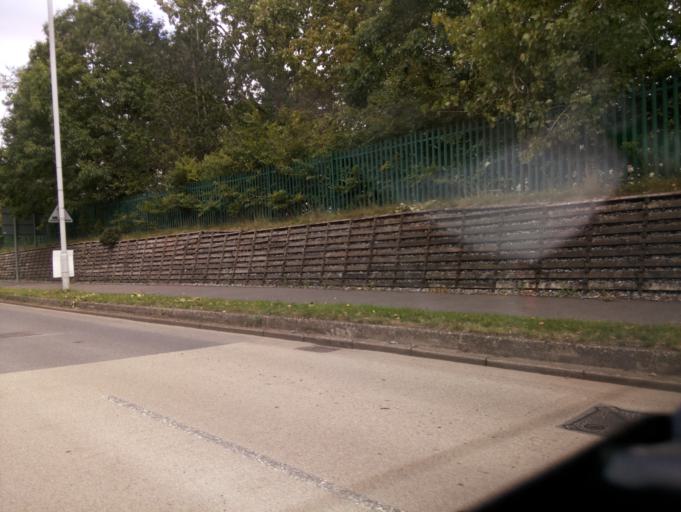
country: GB
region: England
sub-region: Devon
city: Heavitree
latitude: 50.7203
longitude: -3.4791
